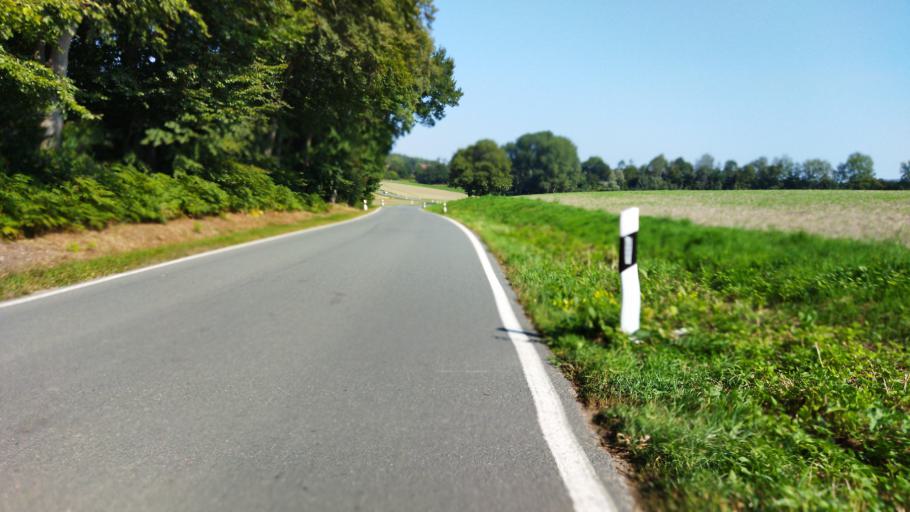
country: DE
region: North Rhine-Westphalia
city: Lengerich
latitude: 52.2271
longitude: 7.8694
